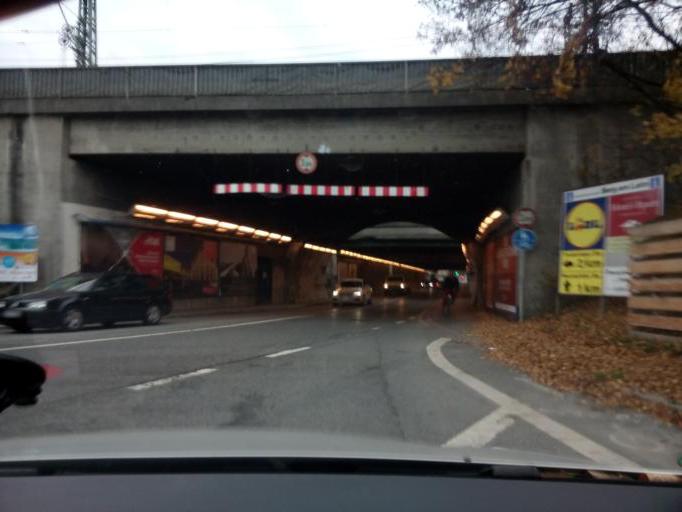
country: DE
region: Bavaria
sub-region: Upper Bavaria
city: Bogenhausen
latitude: 48.1358
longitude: 11.6335
